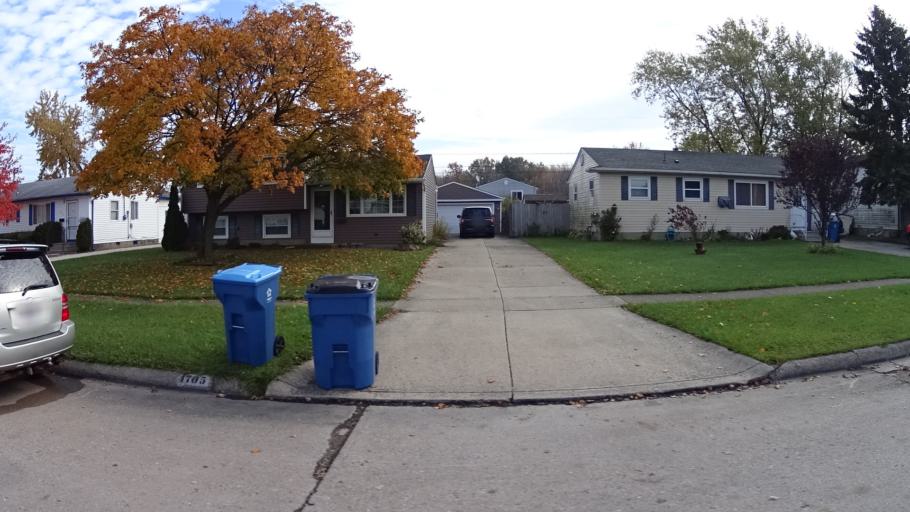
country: US
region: Ohio
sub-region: Lorain County
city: Sheffield
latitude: 41.4259
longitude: -82.1089
